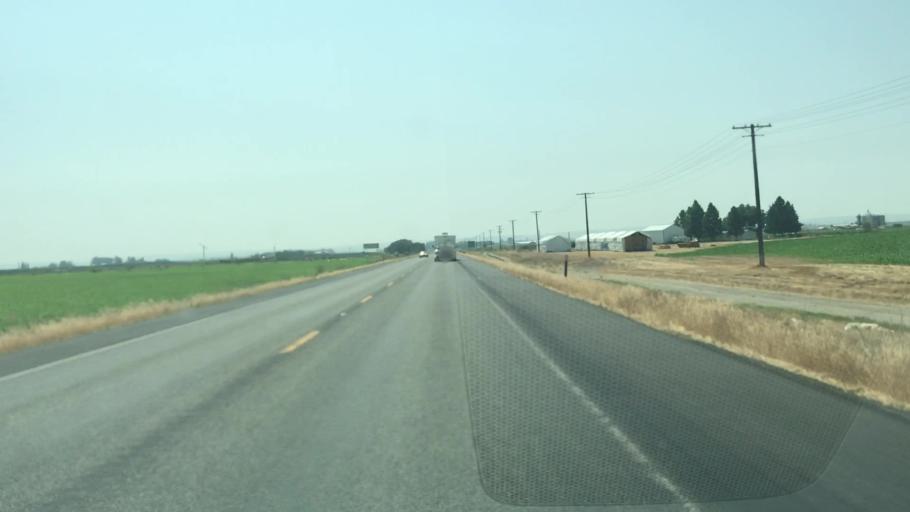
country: US
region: Washington
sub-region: Grant County
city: Quincy
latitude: 47.1283
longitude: -119.8536
